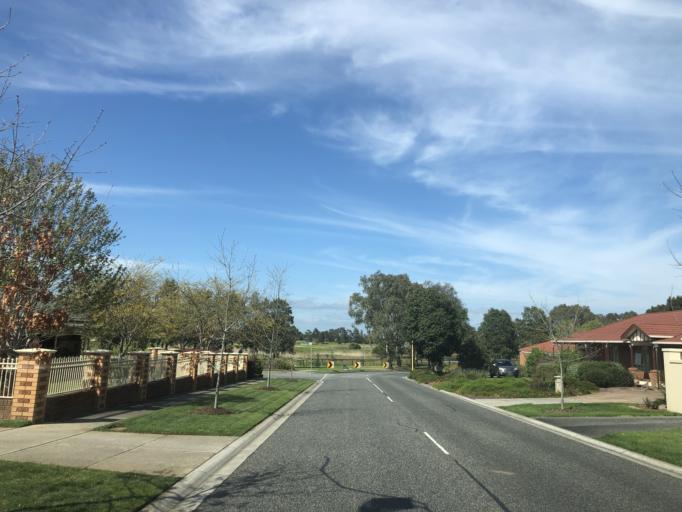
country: AU
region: Victoria
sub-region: Casey
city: Narre Warren North
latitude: -37.9942
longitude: 145.2915
